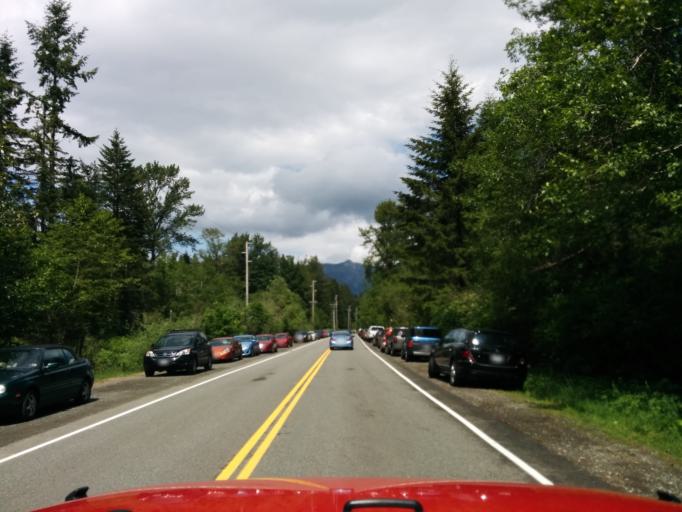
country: US
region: Washington
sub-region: King County
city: Riverbend
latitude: 47.4367
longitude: -121.7673
